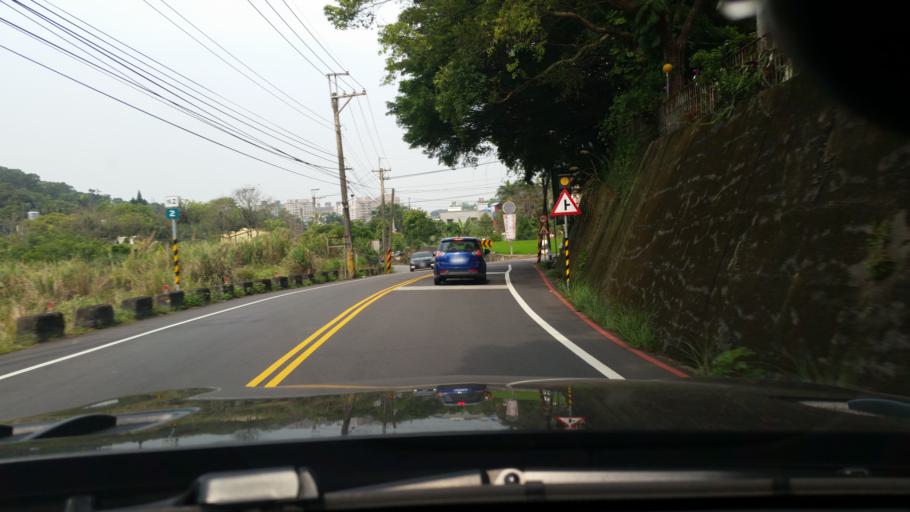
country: TW
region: Taiwan
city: Taoyuan City
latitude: 25.0617
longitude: 121.3076
